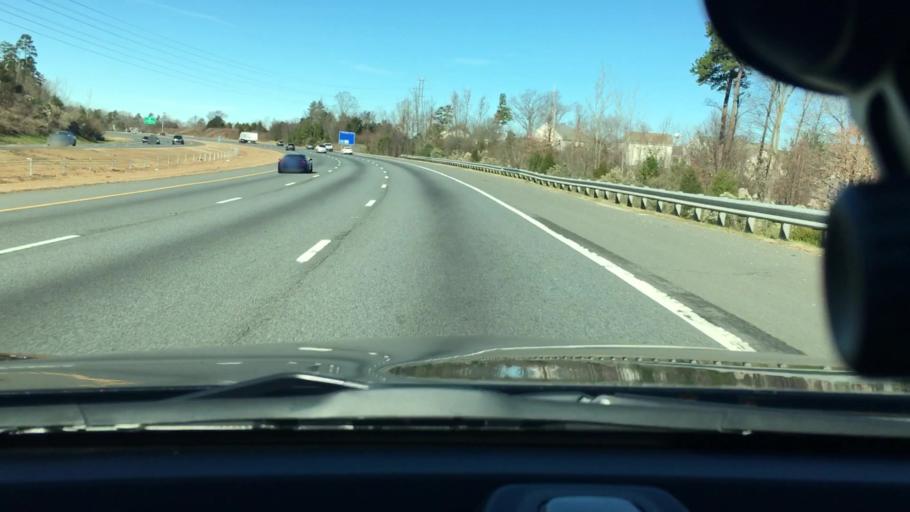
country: US
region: North Carolina
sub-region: Cabarrus County
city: Harrisburg
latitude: 35.3027
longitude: -80.6864
